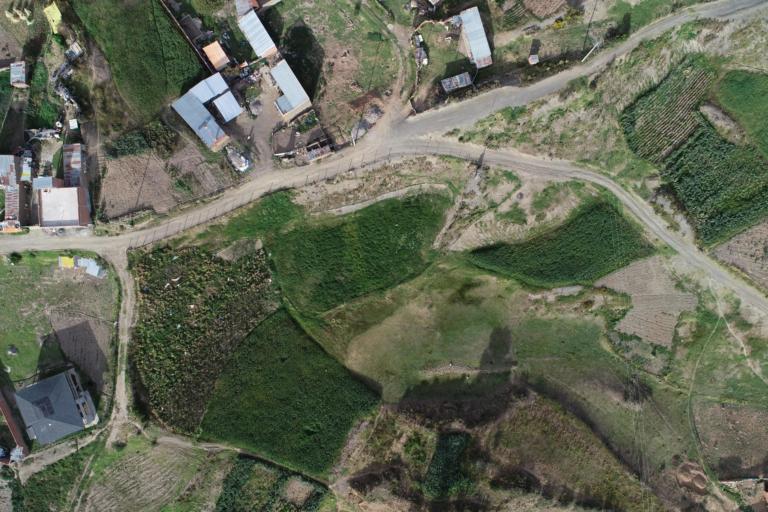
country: BO
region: La Paz
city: La Paz
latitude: -16.5469
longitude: -68.0003
